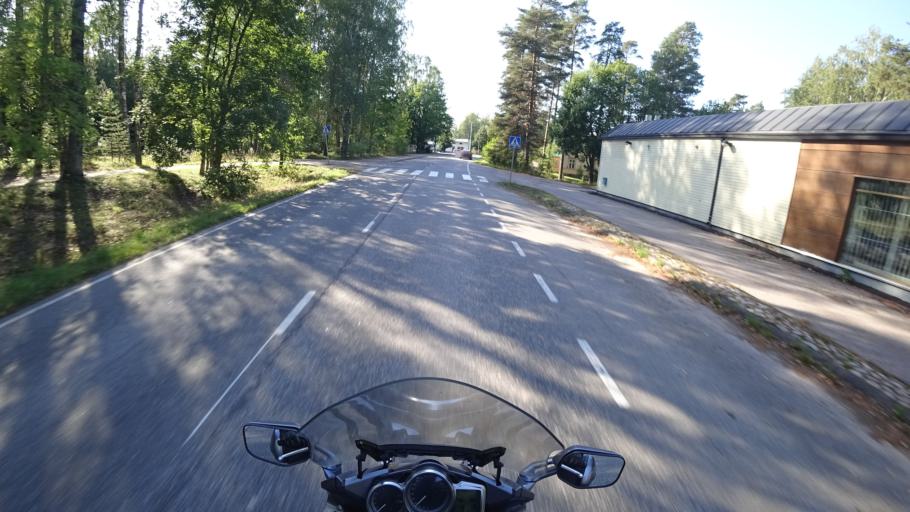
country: FI
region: Uusimaa
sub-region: Helsinki
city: Sammatti
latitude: 60.3181
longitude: 23.8256
